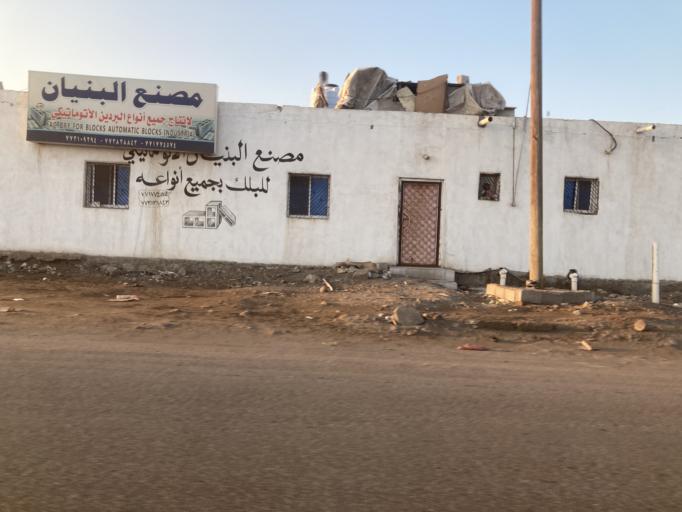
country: YE
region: Aden
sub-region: Ash Shaikh Outhman
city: Ash Shaykh `Uthman
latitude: 12.8636
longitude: 45.0184
